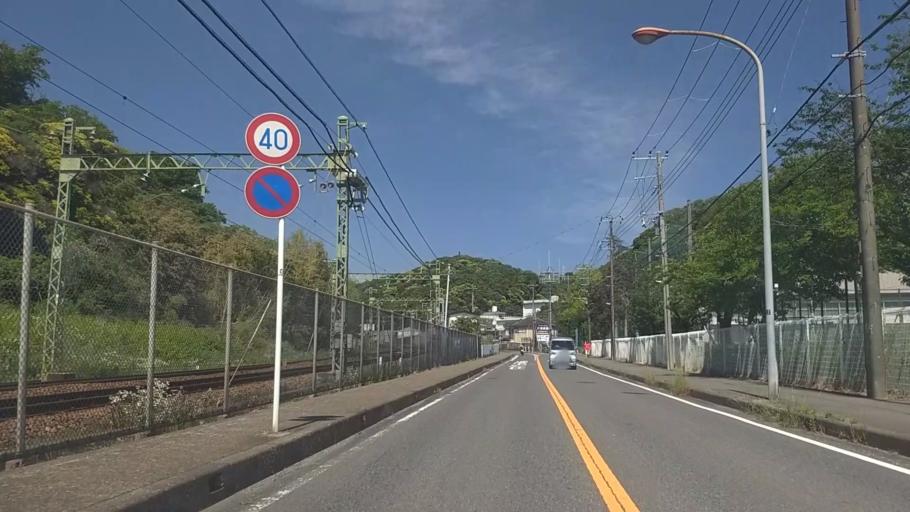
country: JP
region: Kanagawa
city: Zushi
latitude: 35.3092
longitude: 139.5978
